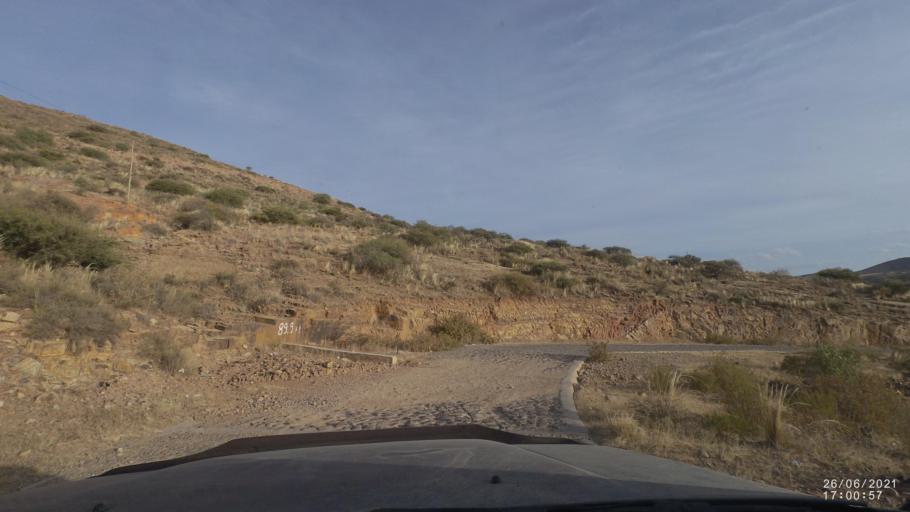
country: BO
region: Cochabamba
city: Cliza
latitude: -17.6632
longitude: -65.9096
